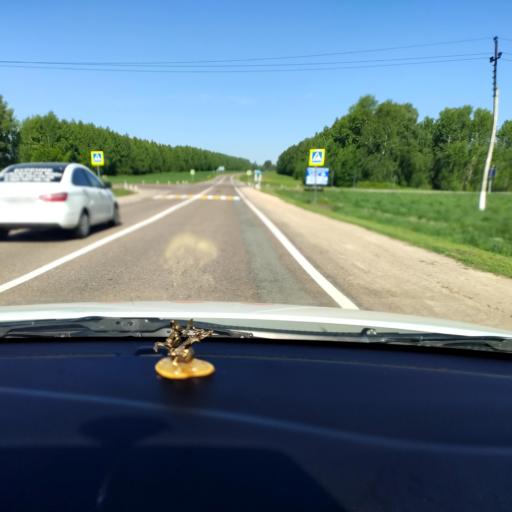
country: RU
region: Tatarstan
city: Vysokaya Gora
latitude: 56.0336
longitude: 49.2378
